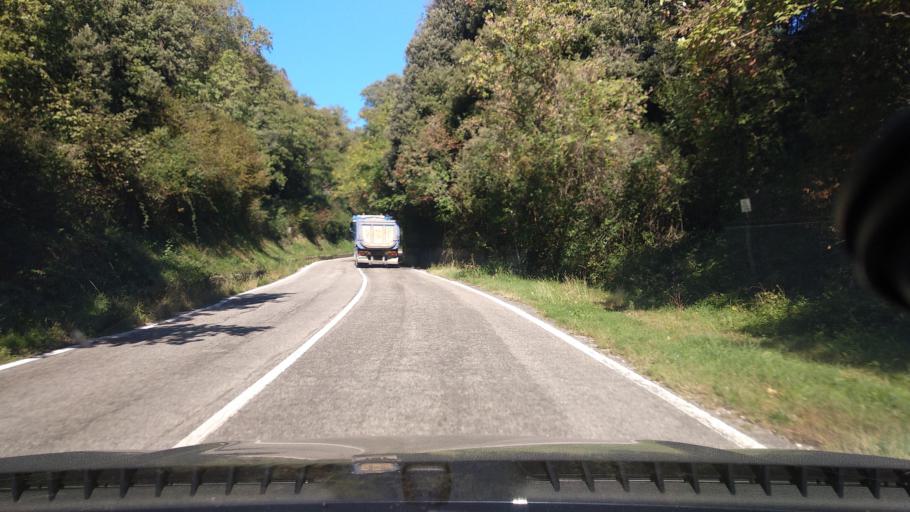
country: IT
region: Veneto
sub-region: Provincia di Verona
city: Garda
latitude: 45.5871
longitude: 10.6996
